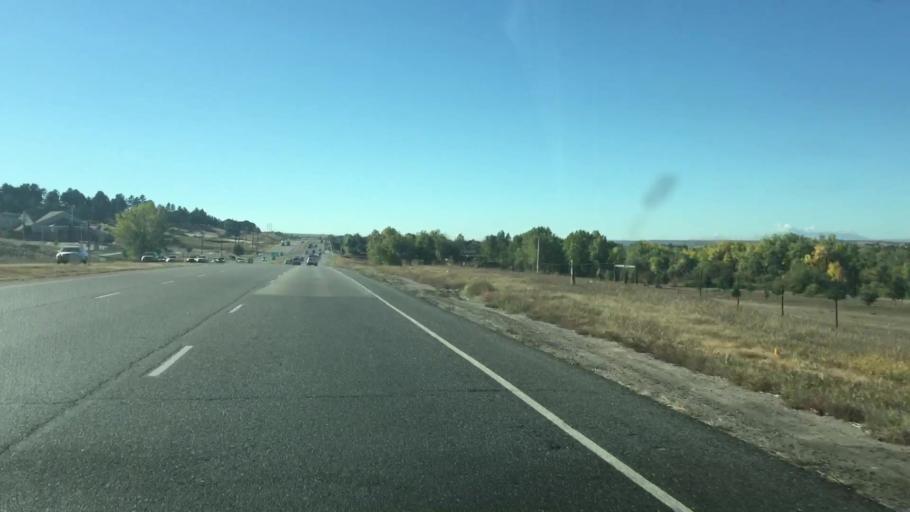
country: US
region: Colorado
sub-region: Douglas County
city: Parker
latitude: 39.5056
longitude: -104.7631
